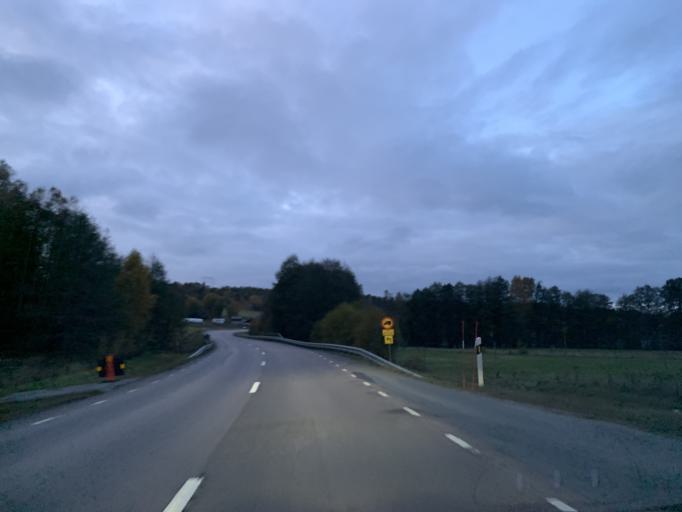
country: SE
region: Stockholm
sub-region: Botkyrka Kommun
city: Varsta
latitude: 59.1154
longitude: 17.8056
